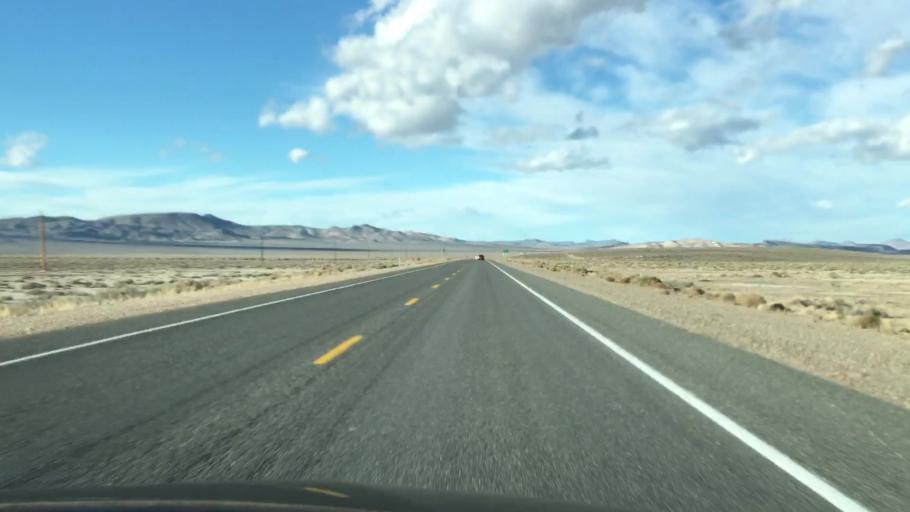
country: US
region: Nevada
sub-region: Esmeralda County
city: Goldfield
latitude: 37.4547
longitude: -117.1702
